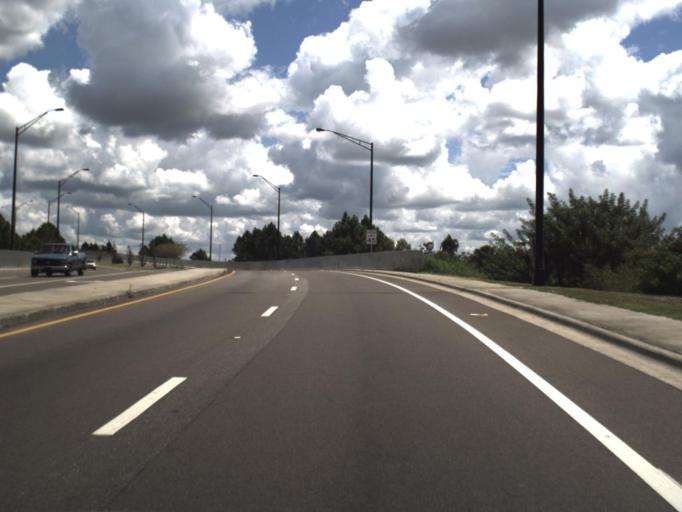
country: US
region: Florida
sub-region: Polk County
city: Lakeland
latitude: 28.0434
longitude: -81.9697
